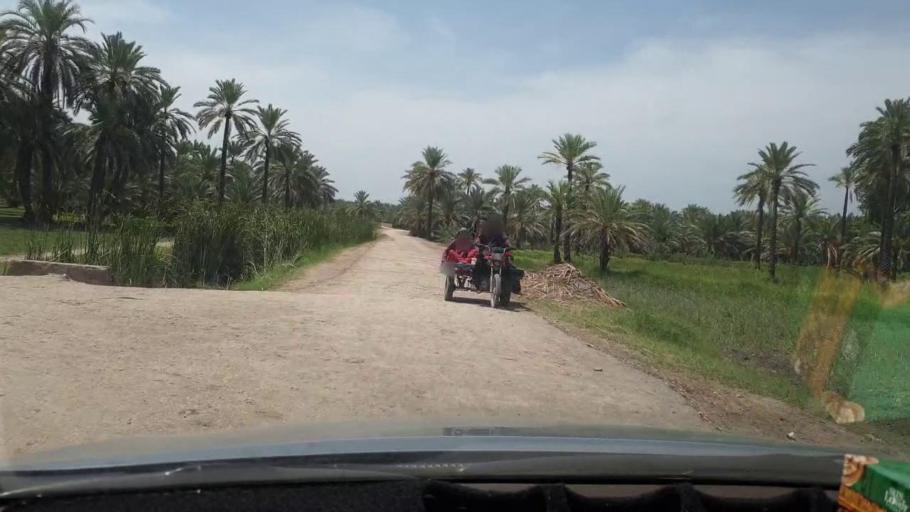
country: PK
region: Sindh
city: Khairpur
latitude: 27.4829
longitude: 68.7729
